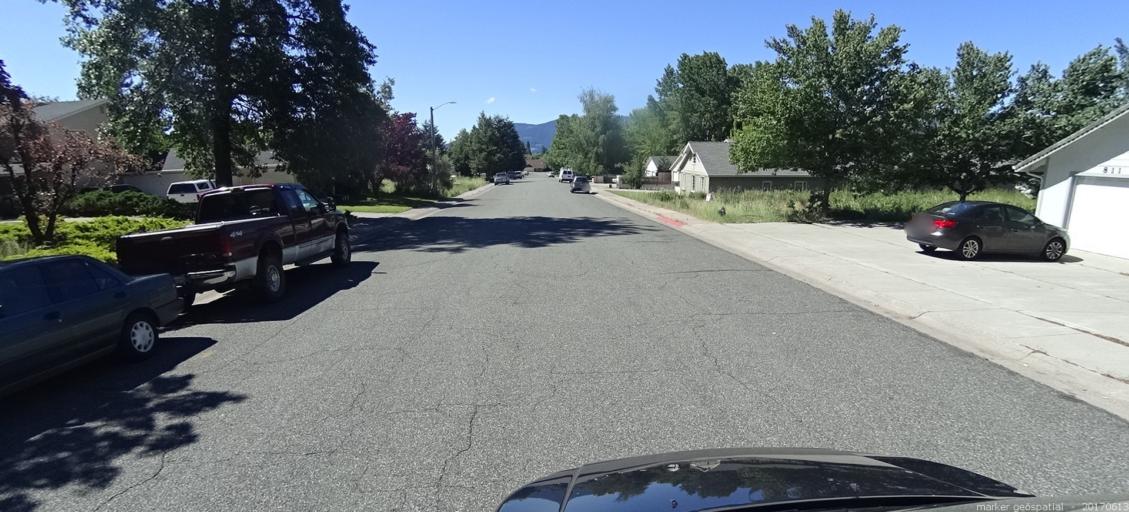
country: US
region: California
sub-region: Siskiyou County
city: Mount Shasta
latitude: 41.3226
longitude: -122.3128
